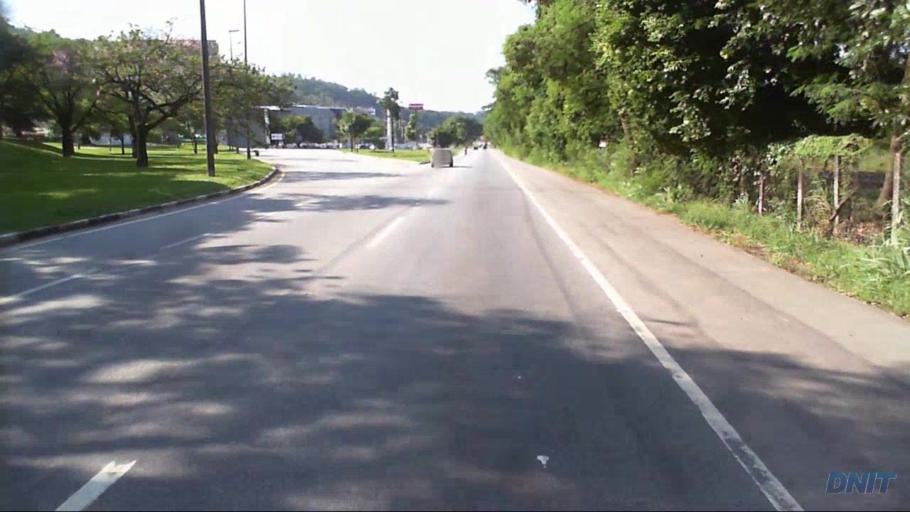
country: BR
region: Minas Gerais
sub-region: Ipatinga
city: Ipatinga
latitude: -19.5003
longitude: -42.5664
